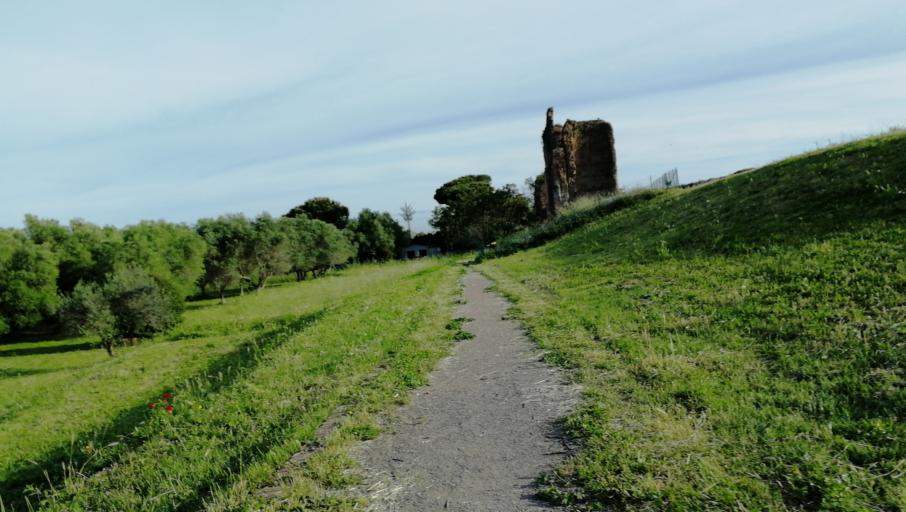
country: IT
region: Latium
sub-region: Citta metropolitana di Roma Capitale
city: Rome
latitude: 41.8588
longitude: 12.5435
